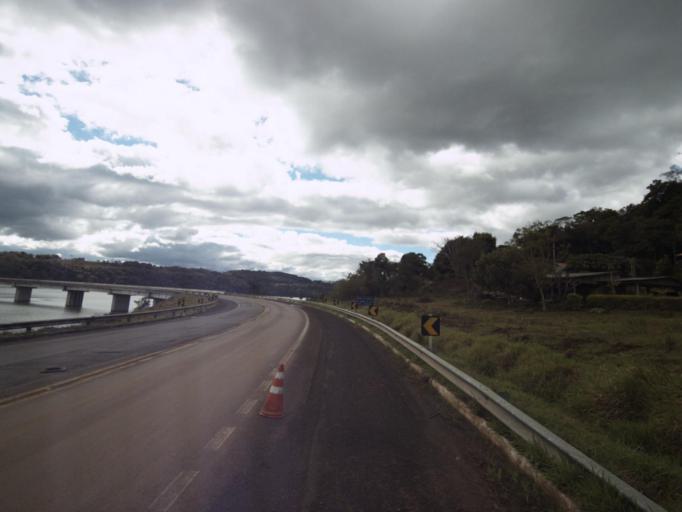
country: BR
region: Santa Catarina
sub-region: Concordia
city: Concordia
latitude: -27.3803
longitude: -51.9859
